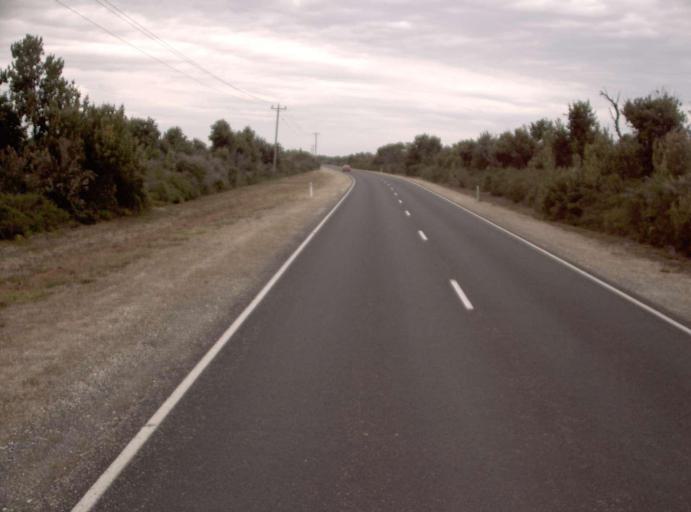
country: AU
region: Victoria
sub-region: Wellington
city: Sale
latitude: -38.1947
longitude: 147.3631
